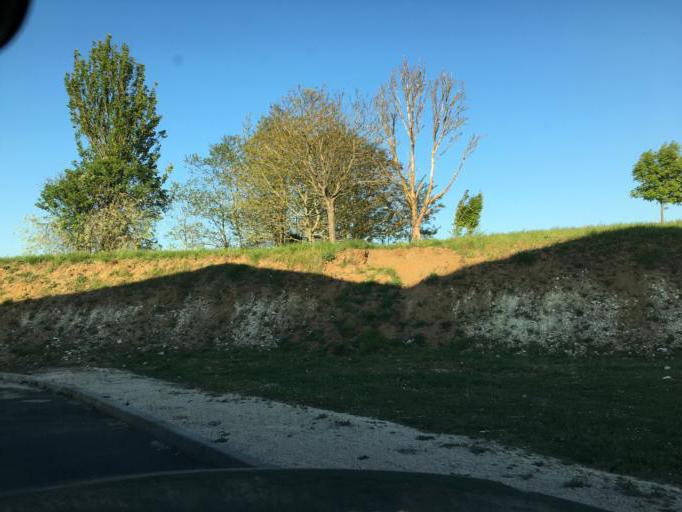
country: FR
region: Centre
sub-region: Departement du Loiret
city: Tavers
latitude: 47.7664
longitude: 1.6153
